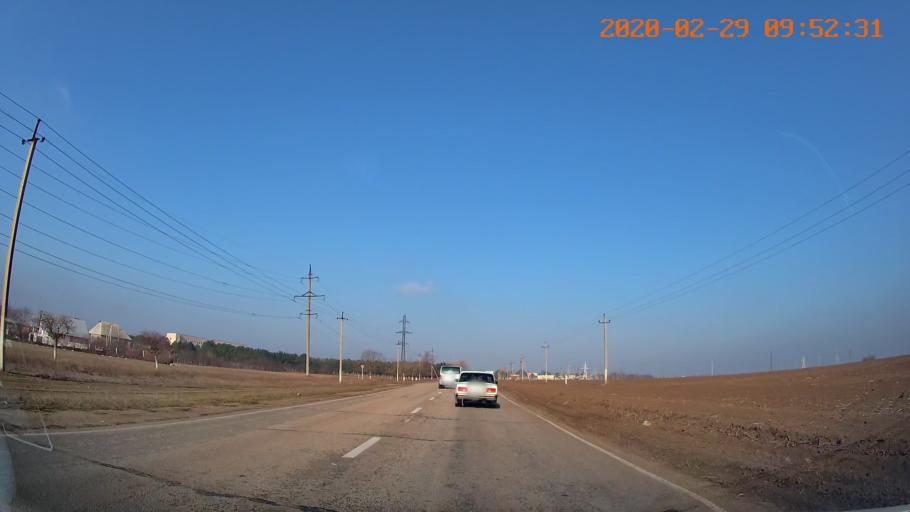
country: MD
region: Telenesti
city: Slobozia
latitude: 46.7164
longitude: 29.7299
